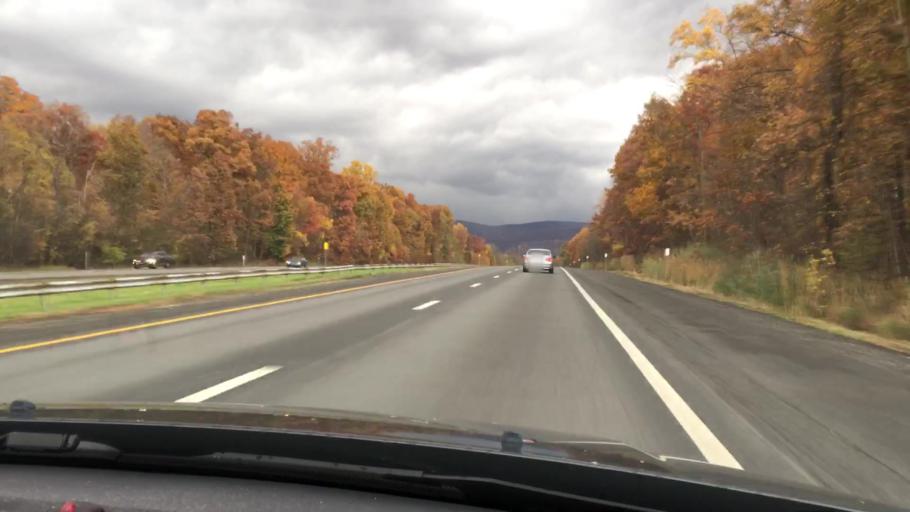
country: US
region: New York
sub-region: Orange County
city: Vails Gate
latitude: 41.4638
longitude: -74.0693
